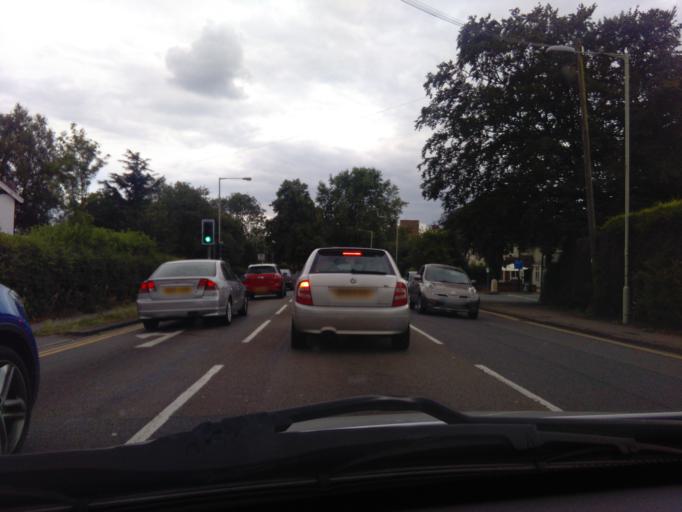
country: GB
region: England
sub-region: Bedford
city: Bedford
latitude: 52.1479
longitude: -0.4550
